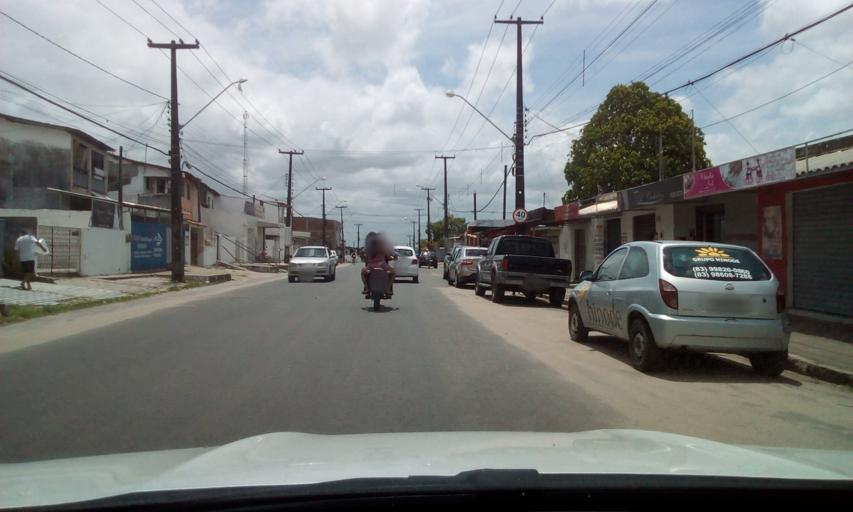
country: BR
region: Paraiba
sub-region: Joao Pessoa
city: Joao Pessoa
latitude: -7.1802
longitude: -34.8816
